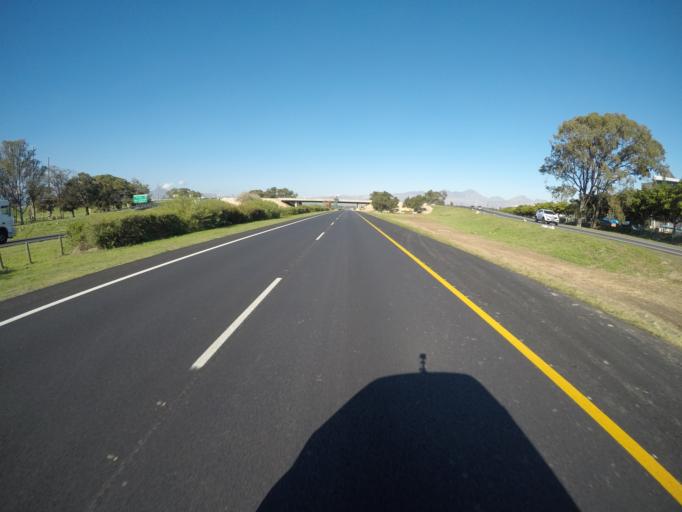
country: ZA
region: Western Cape
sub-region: Cape Winelands District Municipality
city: Stellenbosch
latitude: -34.0757
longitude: 18.8192
